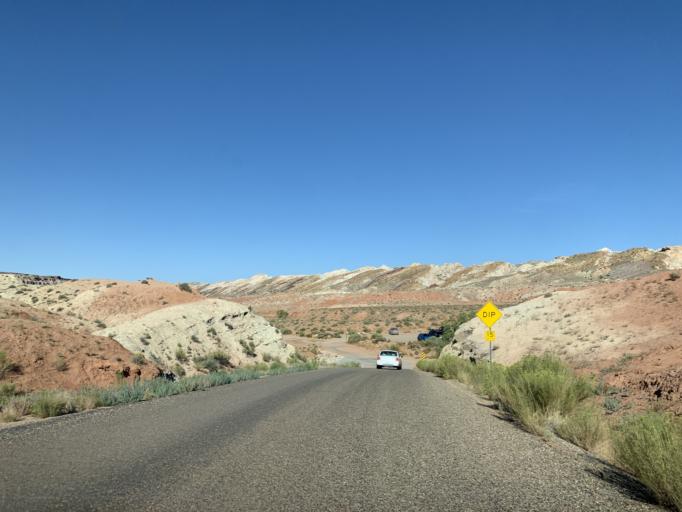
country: US
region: Utah
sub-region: Emery County
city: Ferron
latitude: 38.5824
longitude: -110.8017
